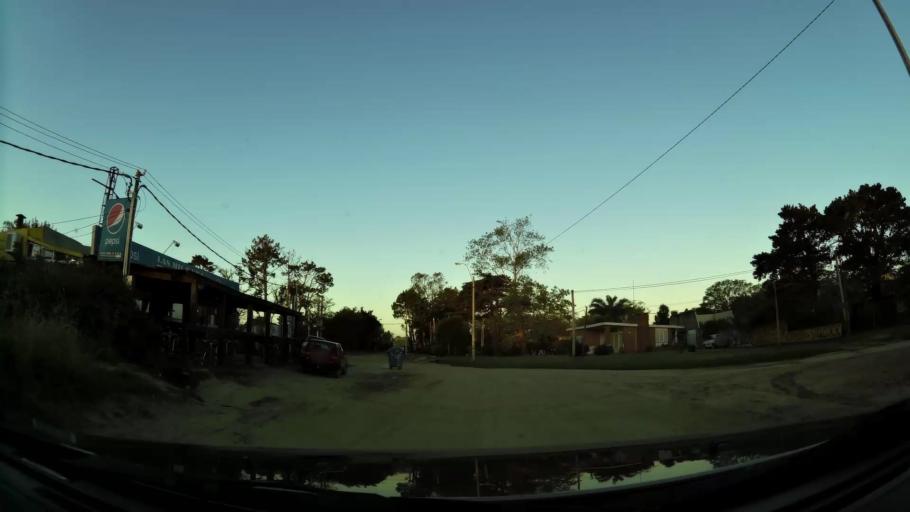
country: UY
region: Canelones
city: Barra de Carrasco
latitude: -34.8412
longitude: -55.9731
